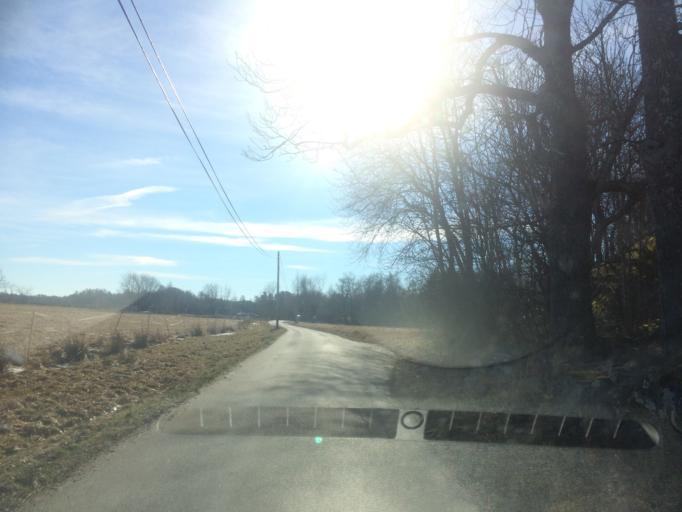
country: SE
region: Vaestra Goetaland
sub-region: Goteborg
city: Torslanda
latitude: 57.7888
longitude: 11.8582
